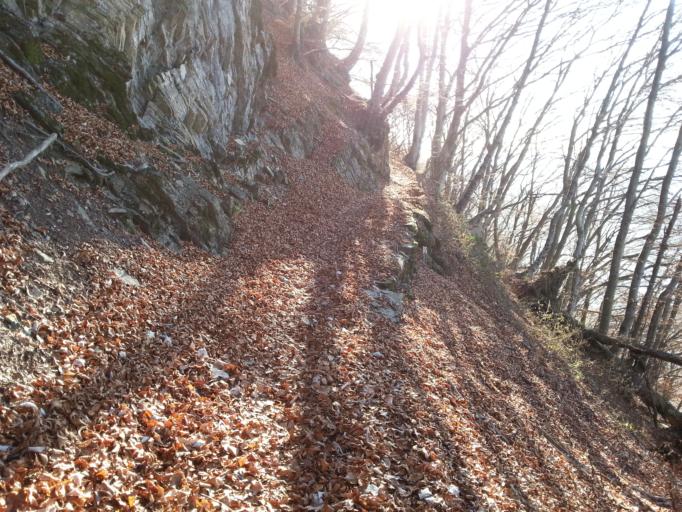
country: CH
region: Ticino
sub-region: Lugano District
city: Cadro
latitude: 46.0262
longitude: 8.9945
